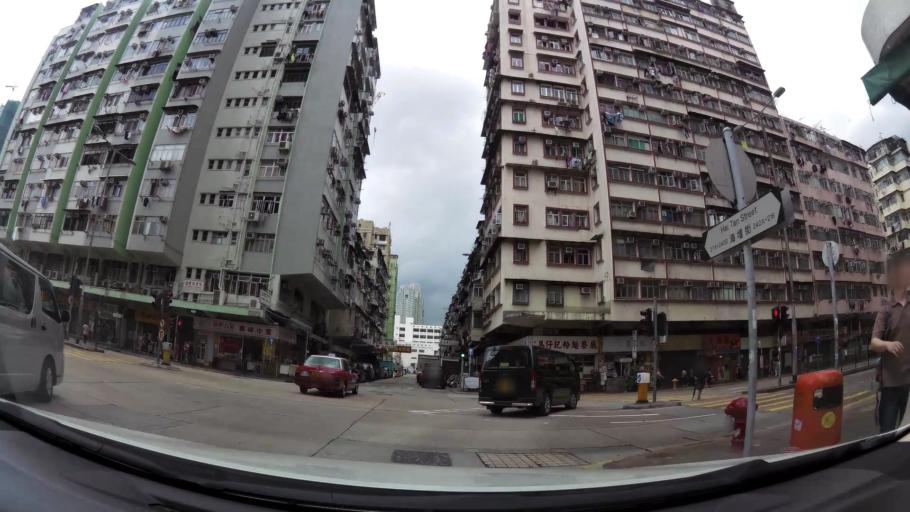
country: HK
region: Sham Shui Po
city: Sham Shui Po
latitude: 22.3286
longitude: 114.1584
